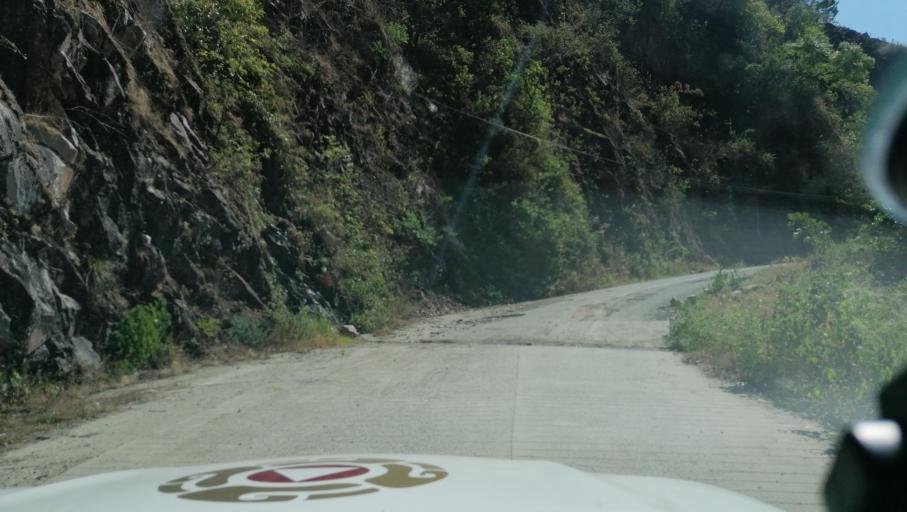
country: MX
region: Chiapas
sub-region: Cacahoatan
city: Benito Juarez
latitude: 15.1851
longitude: -92.1891
